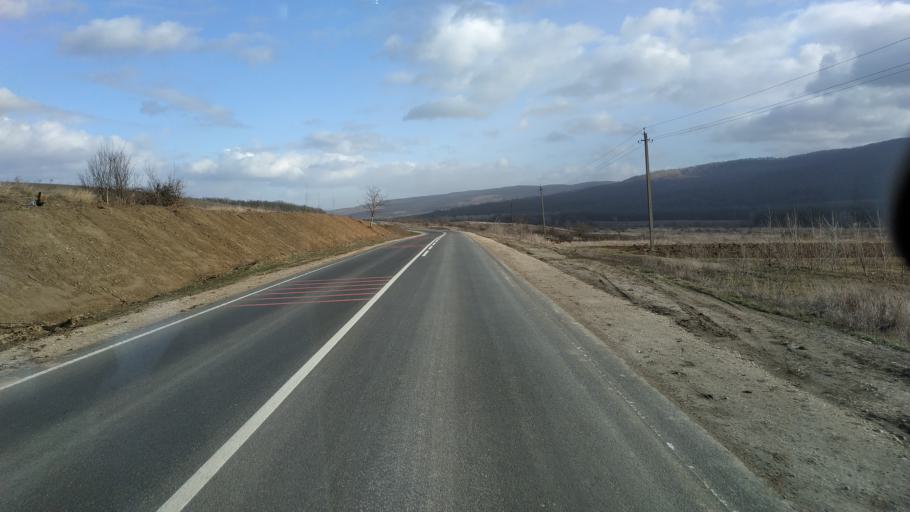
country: MD
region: Calarasi
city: Calarasi
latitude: 47.3148
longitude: 28.1171
